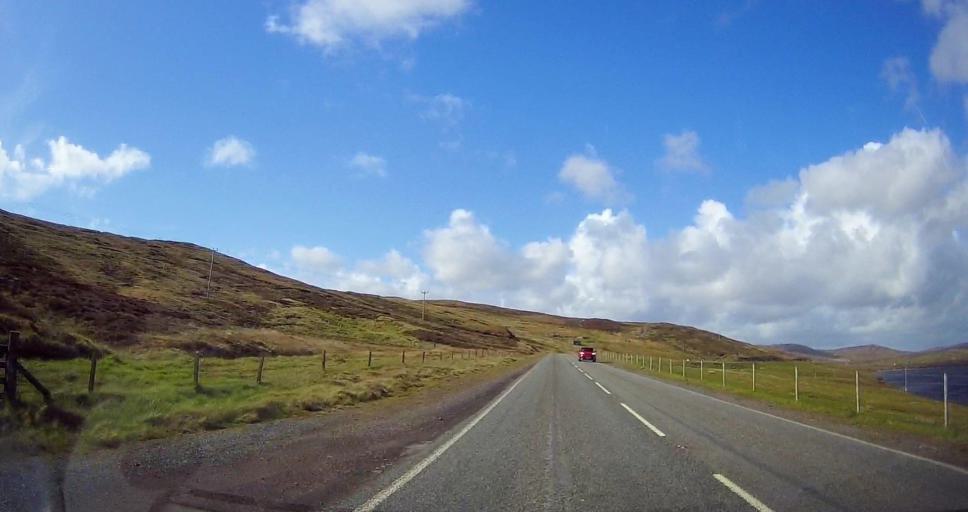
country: GB
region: Scotland
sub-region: Shetland Islands
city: Lerwick
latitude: 60.2522
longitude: -1.2259
